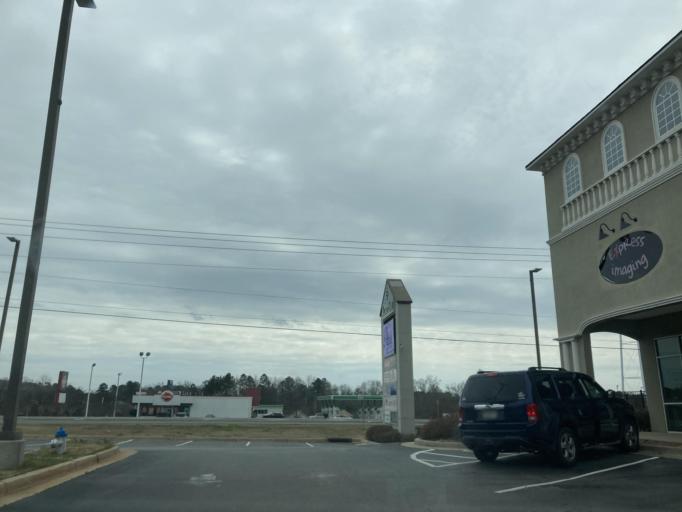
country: US
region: Georgia
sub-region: Jones County
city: Gray
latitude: 33.0036
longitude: -83.5496
